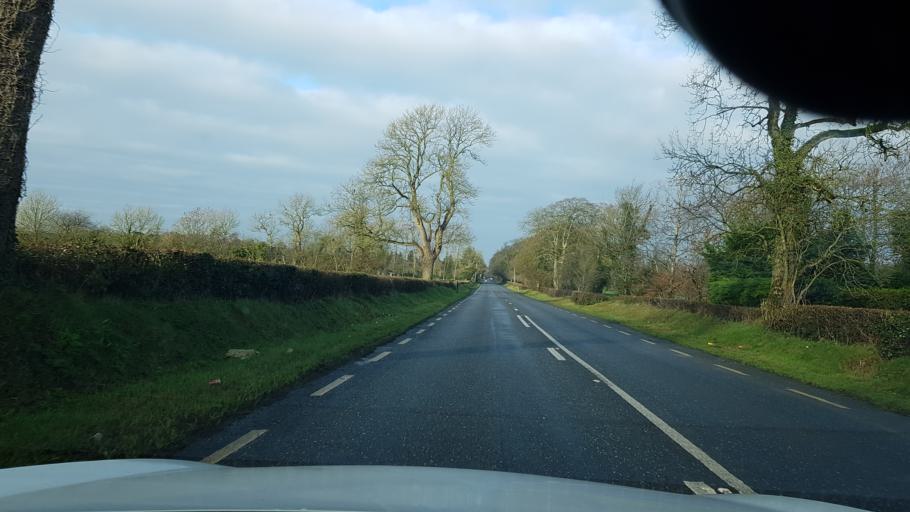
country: IE
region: Leinster
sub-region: An Mhi
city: Navan
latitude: 53.6244
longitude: -6.6506
